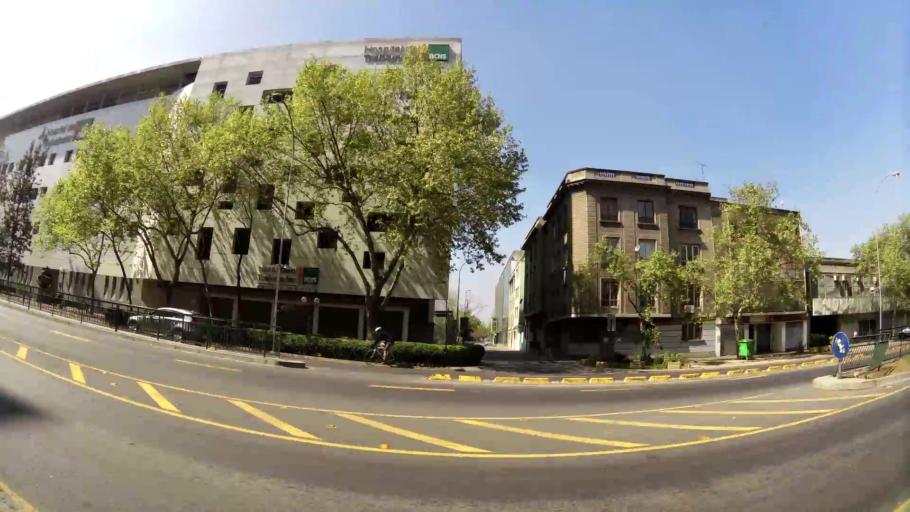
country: CL
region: Santiago Metropolitan
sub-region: Provincia de Santiago
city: Santiago
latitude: -33.4444
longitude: -70.6332
